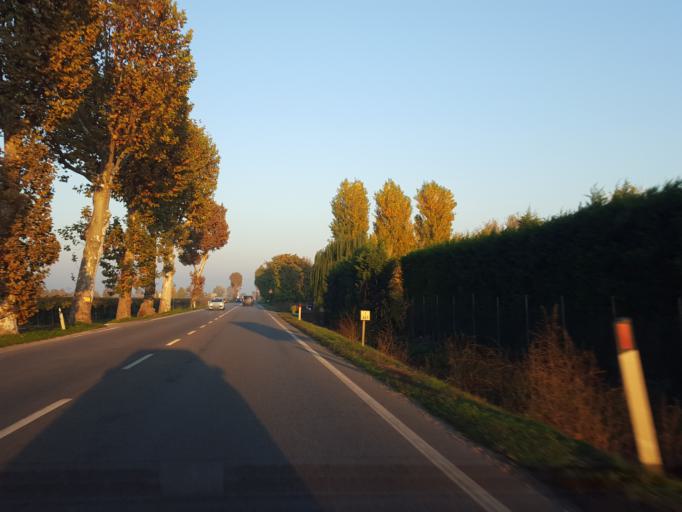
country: IT
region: Veneto
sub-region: Provincia di Verona
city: San Bonifacio
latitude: 45.4087
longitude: 11.3031
